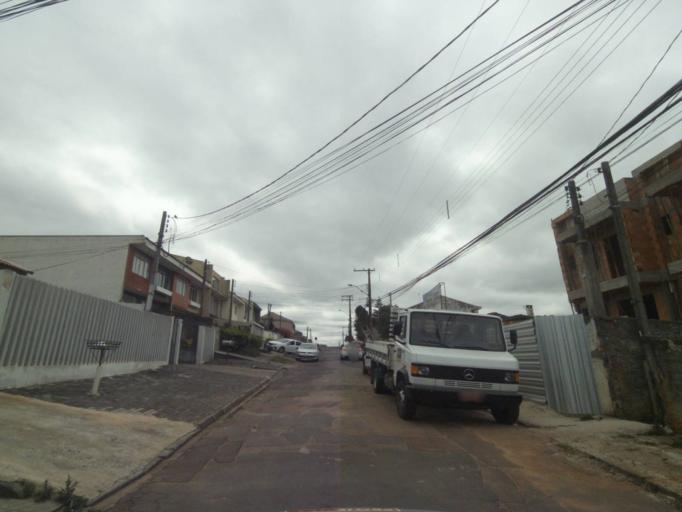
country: BR
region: Parana
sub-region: Pinhais
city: Pinhais
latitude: -25.4819
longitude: -49.2284
